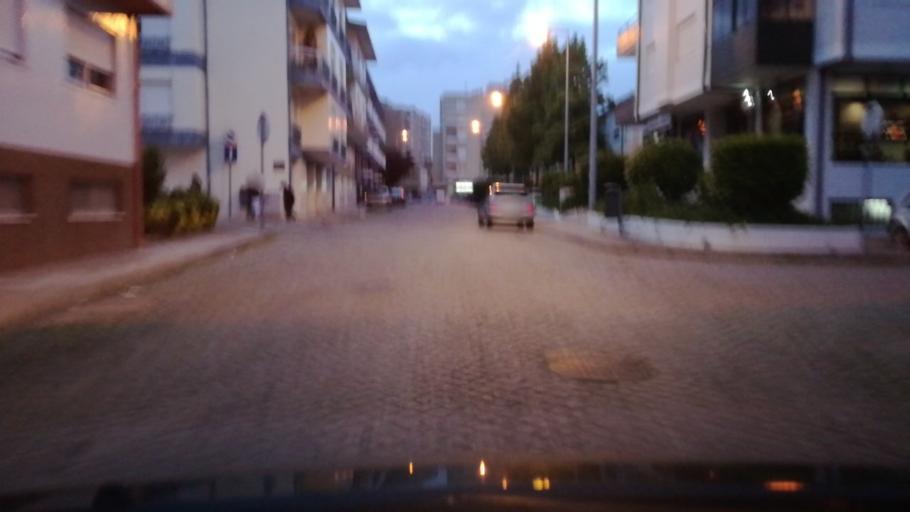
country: PT
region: Porto
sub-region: Maia
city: Anta
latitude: 41.2678
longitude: -8.6101
